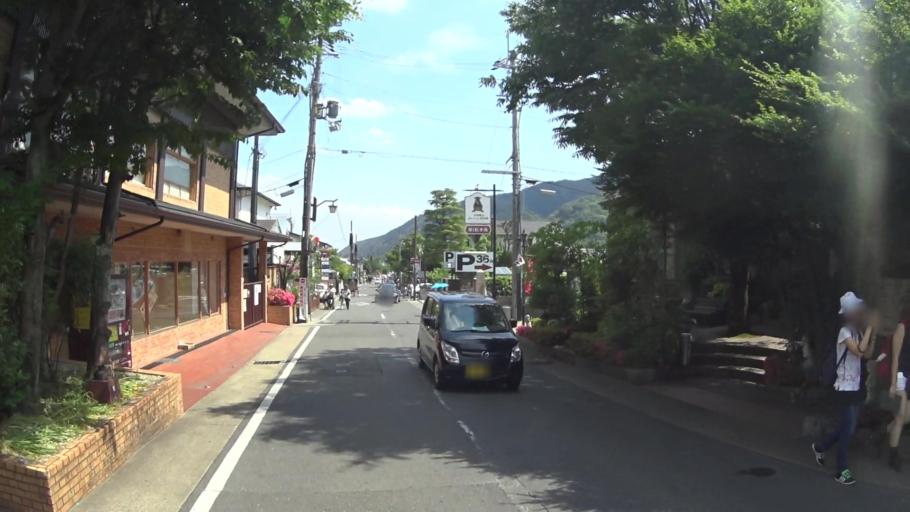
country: JP
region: Kyoto
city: Muko
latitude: 35.0187
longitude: 135.6762
